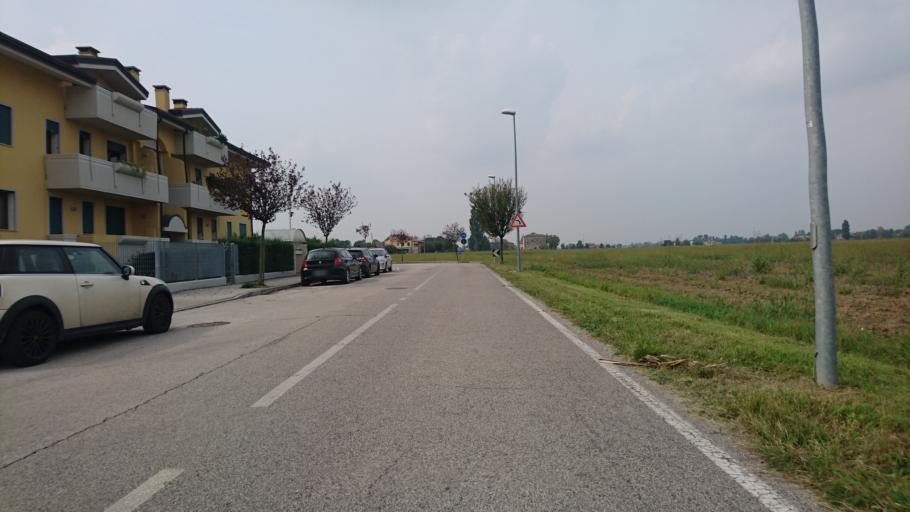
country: IT
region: Veneto
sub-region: Provincia di Padova
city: Tencarola
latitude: 45.4016
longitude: 11.8029
